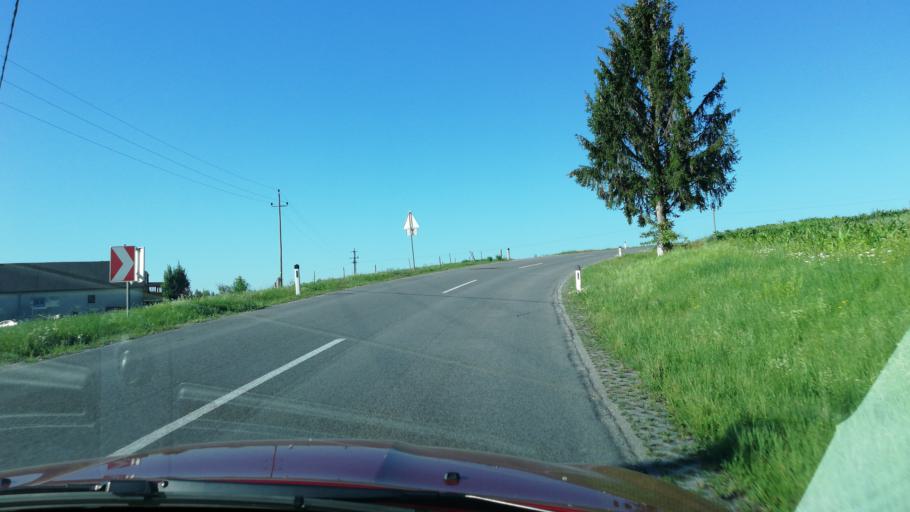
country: AT
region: Upper Austria
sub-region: Politischer Bezirk Urfahr-Umgebung
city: Herzogsdorf
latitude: 48.4639
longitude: 14.0575
